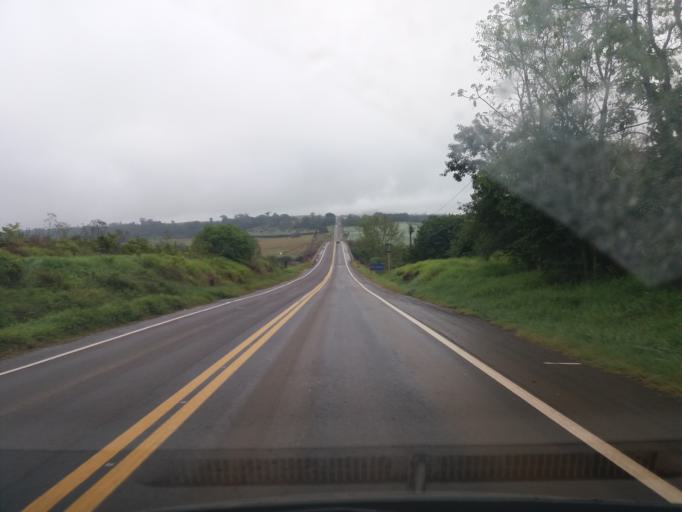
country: BR
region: Parana
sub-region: Realeza
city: Realeza
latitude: -25.5656
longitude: -53.5763
